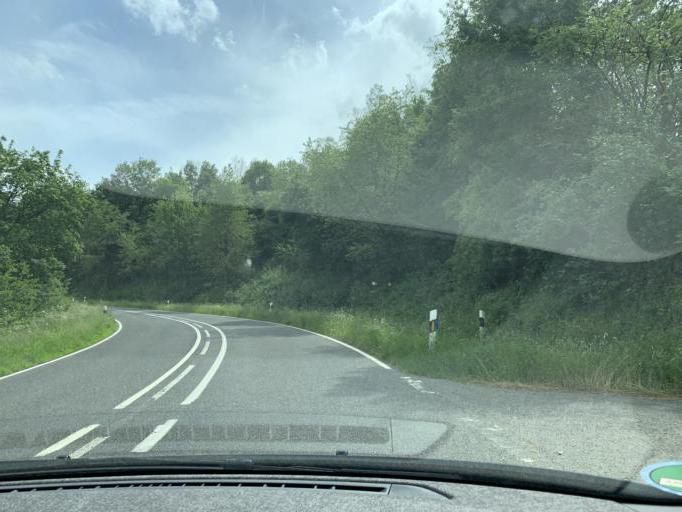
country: DE
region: North Rhine-Westphalia
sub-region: Regierungsbezirk Koln
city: Hurtgenwald
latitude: 50.6831
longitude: 6.4068
